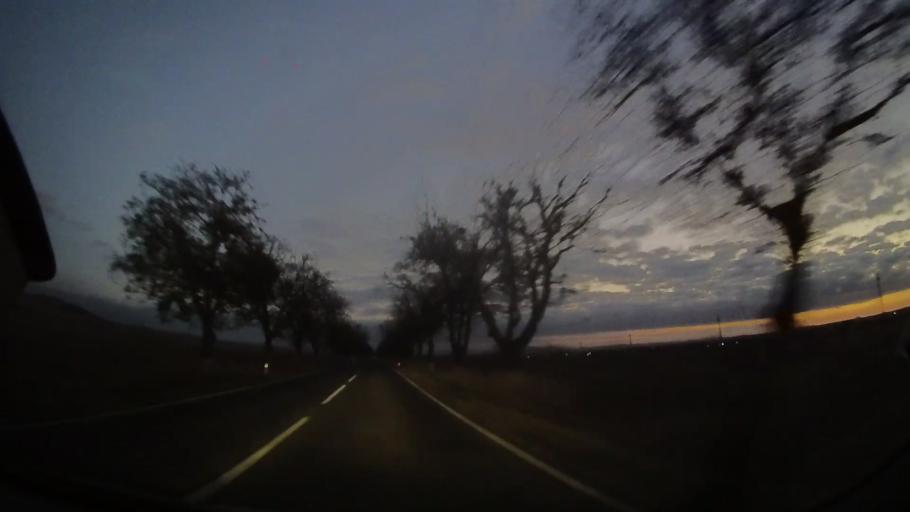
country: RO
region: Tulcea
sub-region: Comuna Frecatei
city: Cataloi
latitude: 45.1018
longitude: 28.7424
